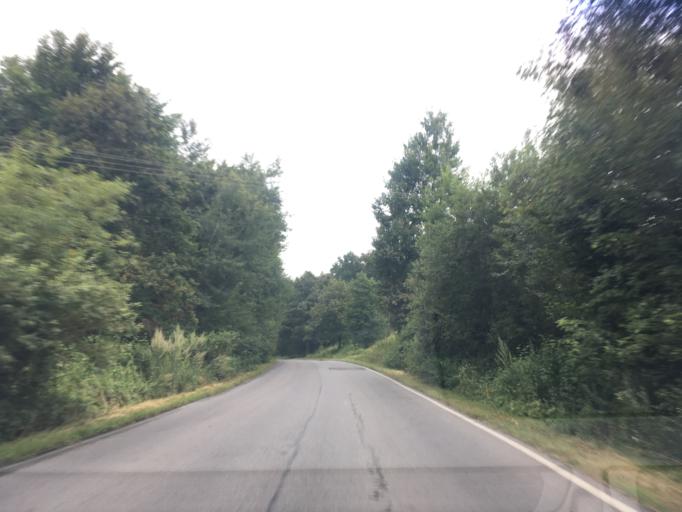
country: PL
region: Lesser Poland Voivodeship
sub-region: Powiat myslenicki
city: Brzaczowice
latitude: 49.8558
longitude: 20.0644
